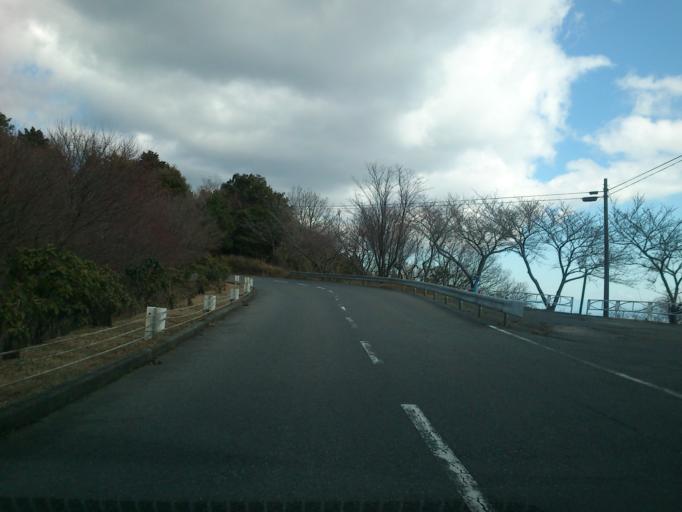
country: JP
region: Shiga Prefecture
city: Otsu-shi
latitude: 35.0389
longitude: 135.8379
